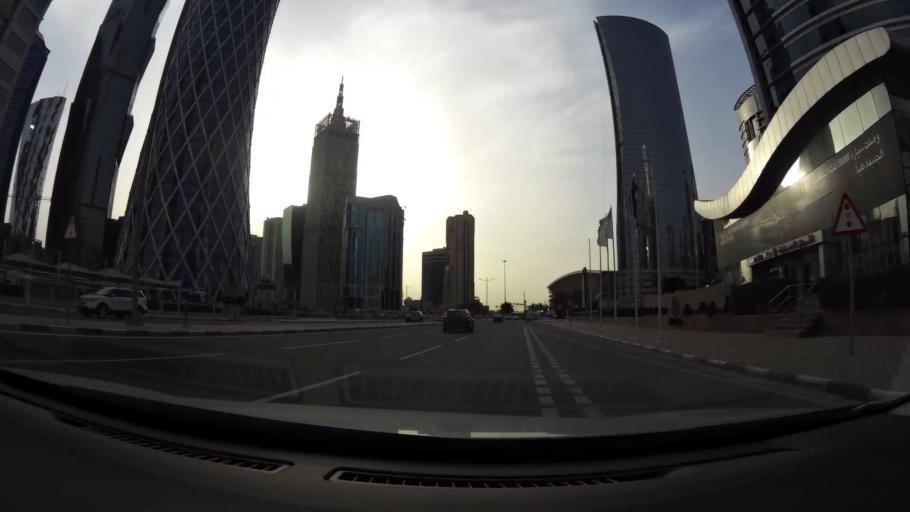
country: QA
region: Baladiyat ad Dawhah
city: Doha
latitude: 25.3201
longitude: 51.5293
